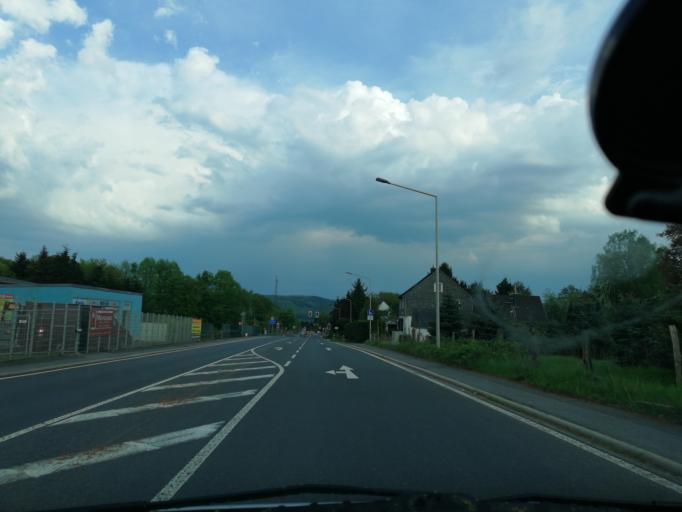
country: DE
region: North Rhine-Westphalia
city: Gevelsberg
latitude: 51.3459
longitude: 7.3395
